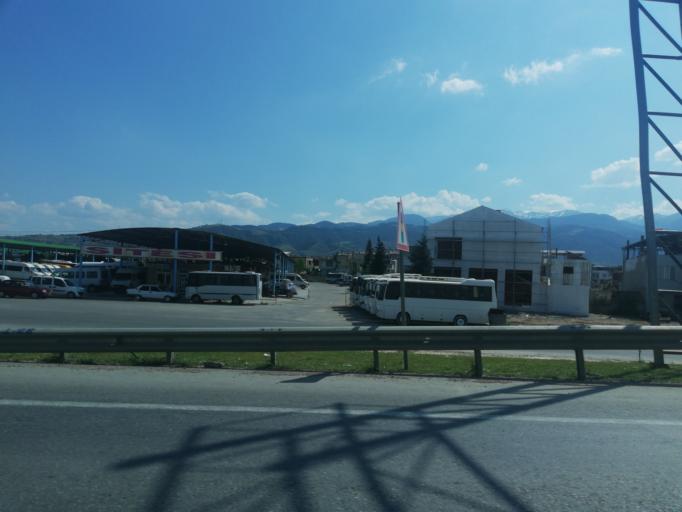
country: TR
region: Manisa
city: Alasehir
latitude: 38.3587
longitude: 28.5414
